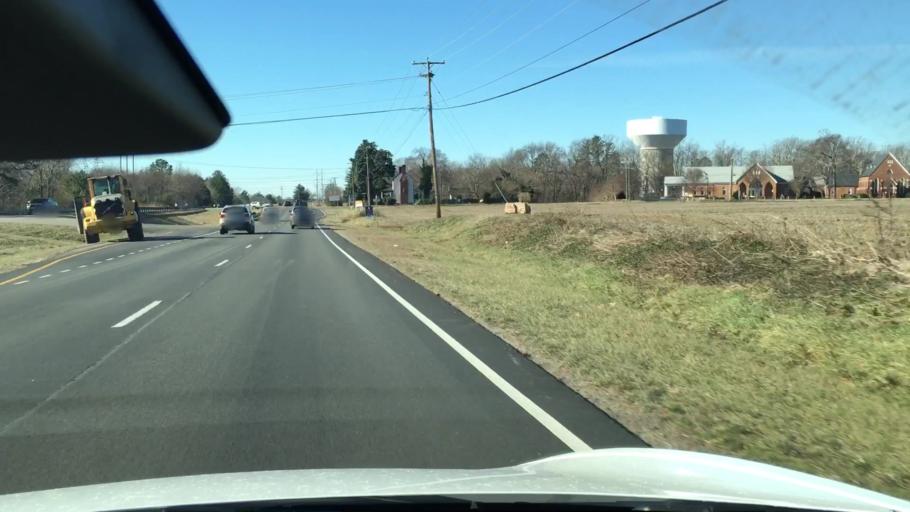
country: US
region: Virginia
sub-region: Chesterfield County
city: Woodlake
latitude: 37.5093
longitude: -77.7082
